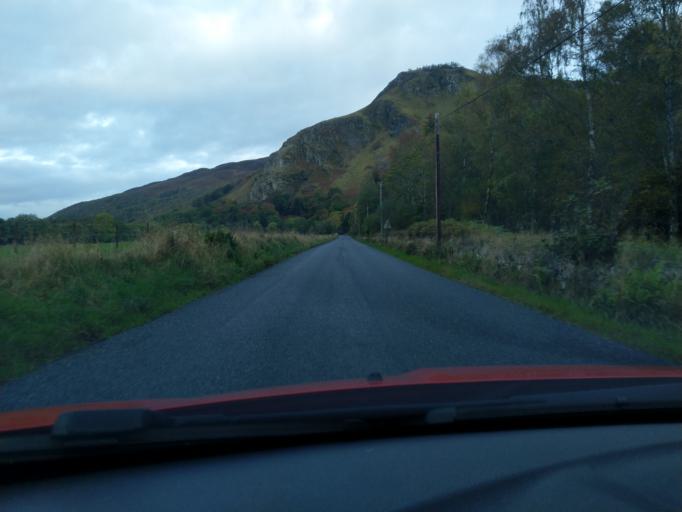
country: GB
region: Scotland
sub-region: Perth and Kinross
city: Aberfeldy
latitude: 56.6992
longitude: -4.1630
